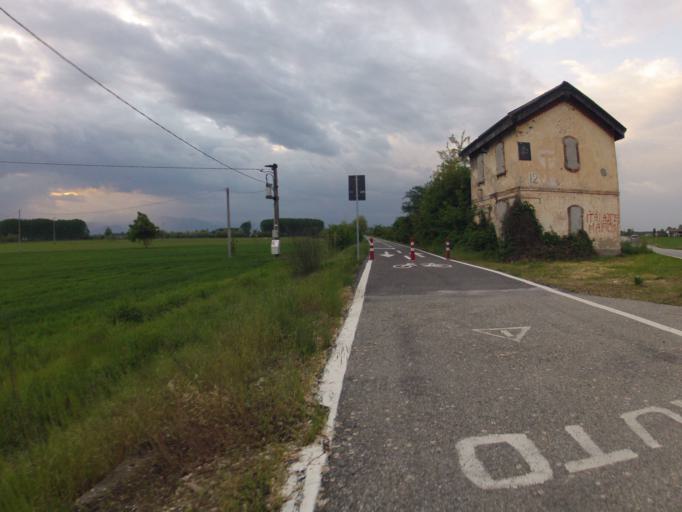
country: IT
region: Piedmont
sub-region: Provincia di Torino
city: Vigone
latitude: 44.8163
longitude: 7.4979
